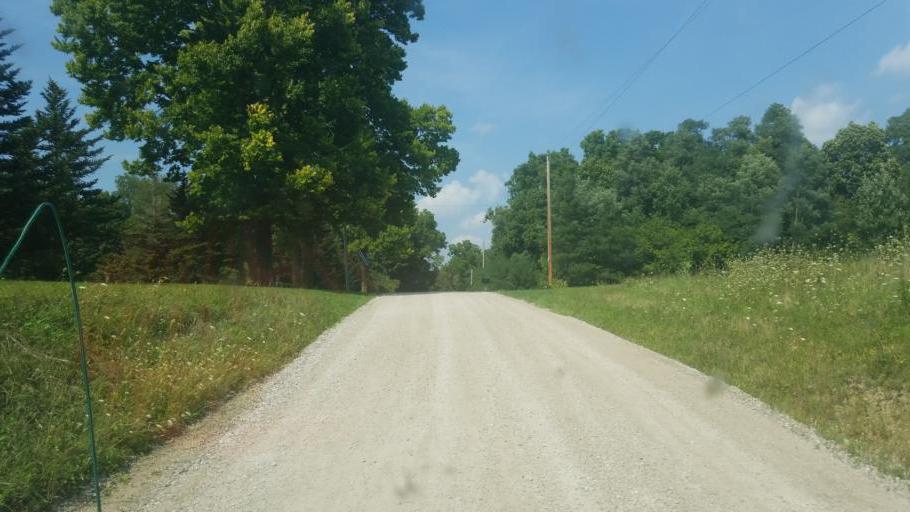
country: US
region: Ohio
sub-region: Huron County
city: New London
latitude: 41.0580
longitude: -82.4097
